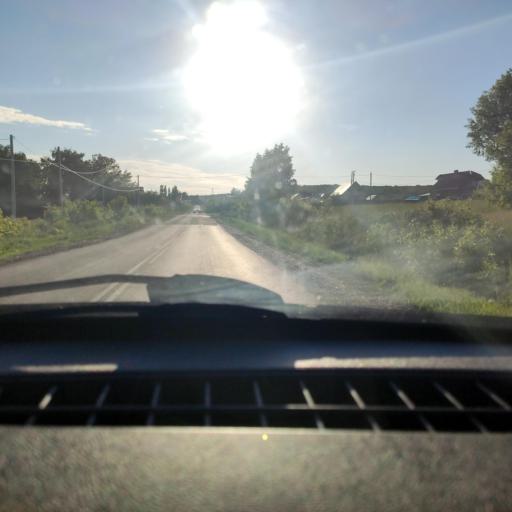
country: RU
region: Bashkortostan
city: Avdon
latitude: 54.6199
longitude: 55.6650
